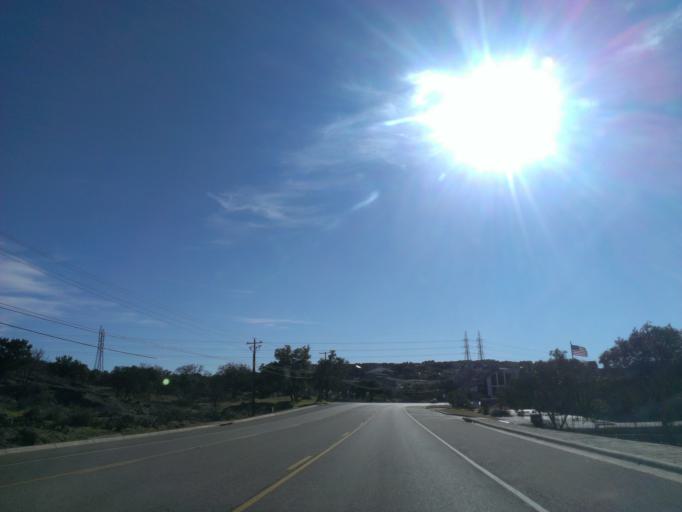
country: US
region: Texas
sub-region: Llano County
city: Horseshoe Bay
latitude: 30.5464
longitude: -98.3468
